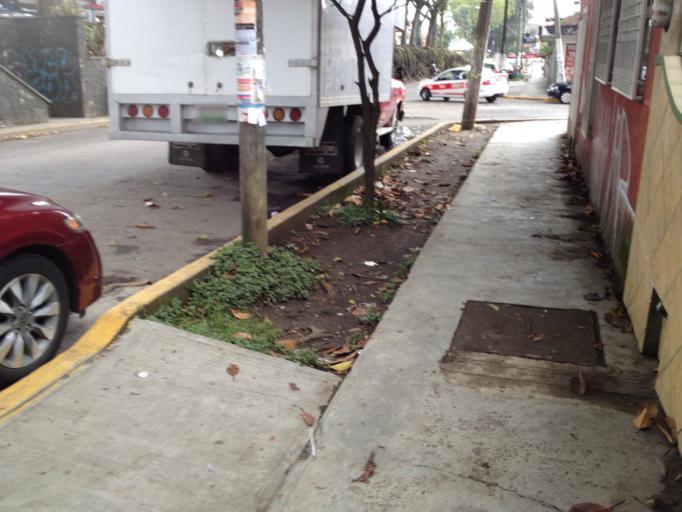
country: MX
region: Veracruz
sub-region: Xalapa
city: Xalapa de Enriquez
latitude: 19.5321
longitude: -96.9077
